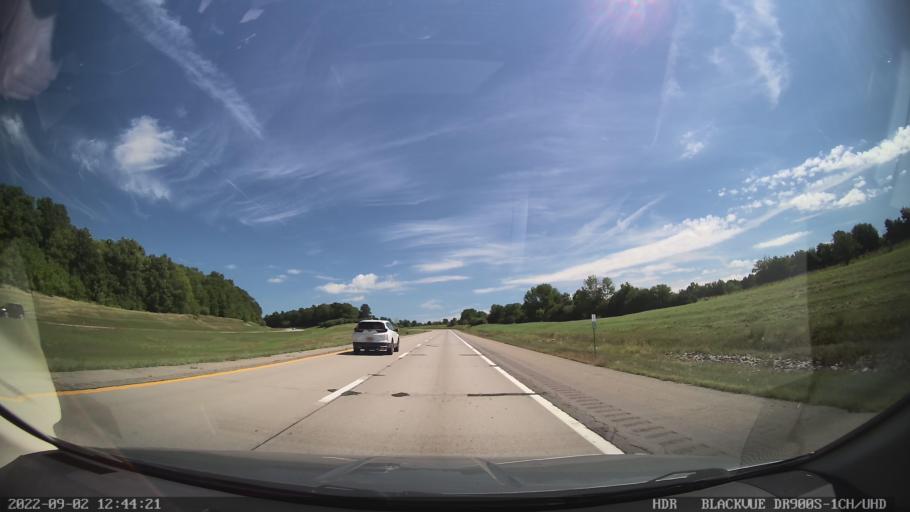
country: US
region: New York
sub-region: Livingston County
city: Geneseo
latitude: 42.7766
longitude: -77.7809
